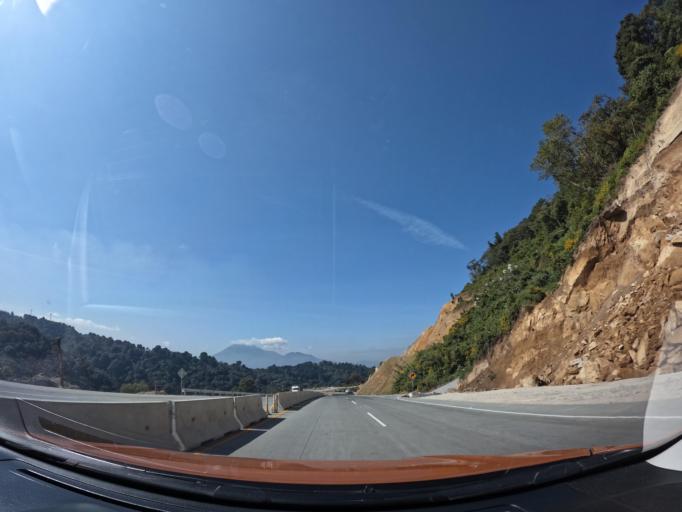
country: GT
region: Guatemala
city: Villa Canales
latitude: 14.4863
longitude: -90.4969
